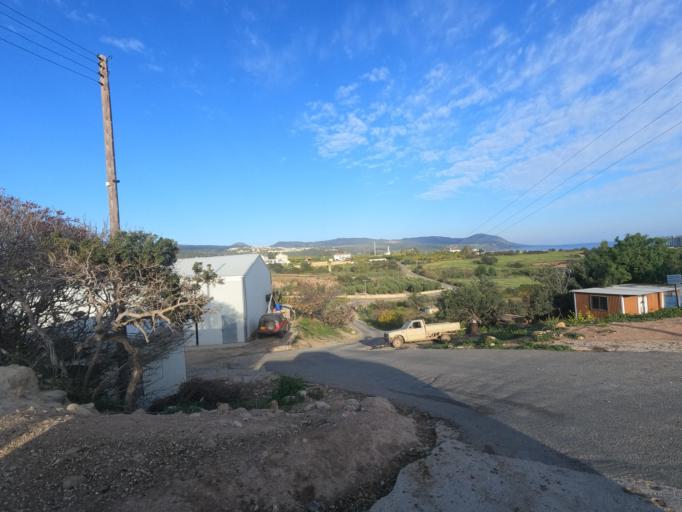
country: CY
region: Pafos
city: Polis
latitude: 35.0328
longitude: 32.3984
